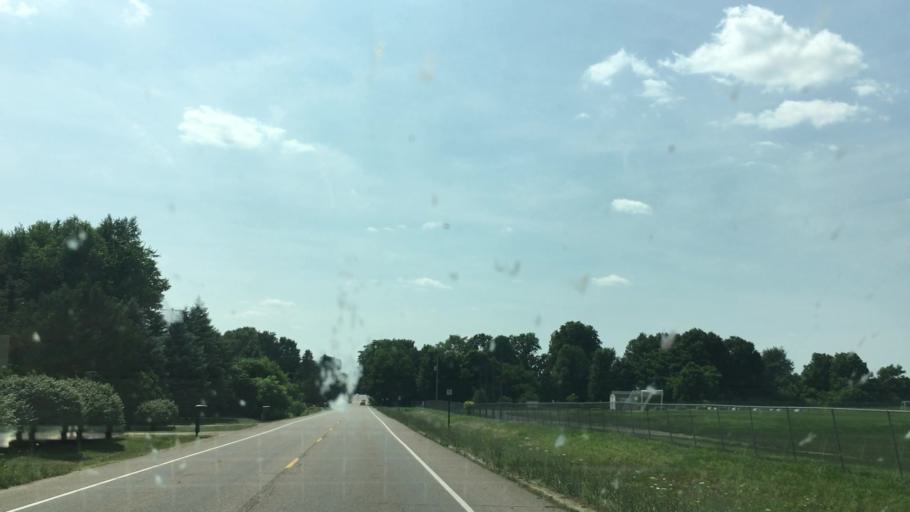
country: US
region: Michigan
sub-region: Allegan County
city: Plainwell
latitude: 42.4645
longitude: -85.6429
